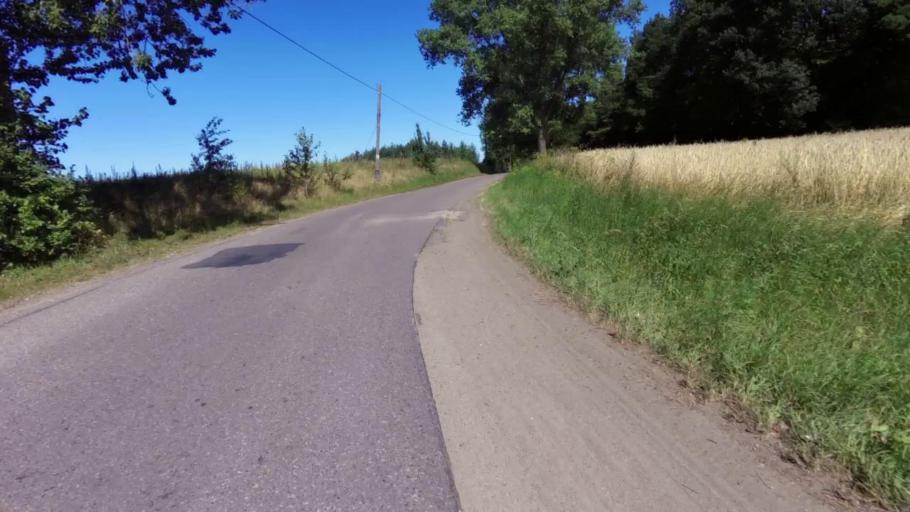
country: PL
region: West Pomeranian Voivodeship
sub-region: Powiat drawski
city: Czaplinek
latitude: 53.5411
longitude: 16.2081
